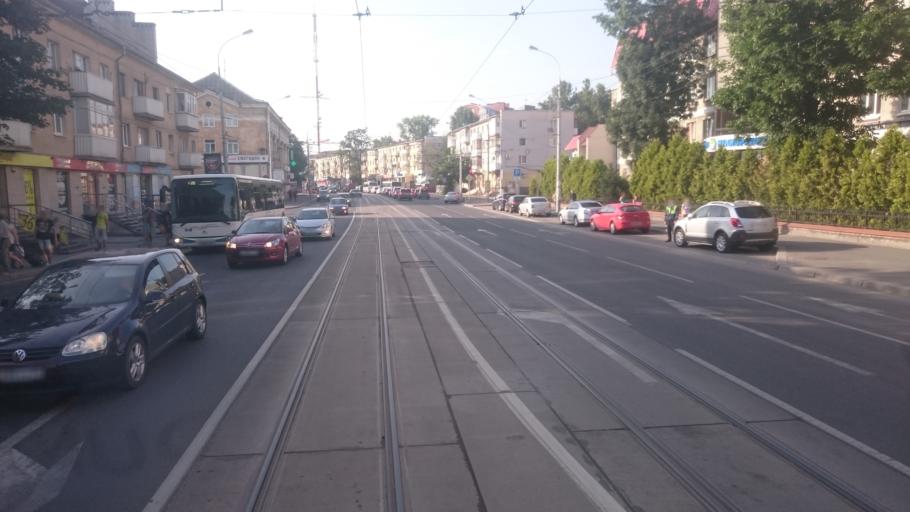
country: RU
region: Kaliningrad
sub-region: Gorod Kaliningrad
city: Kaliningrad
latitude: 54.7234
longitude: 20.4988
